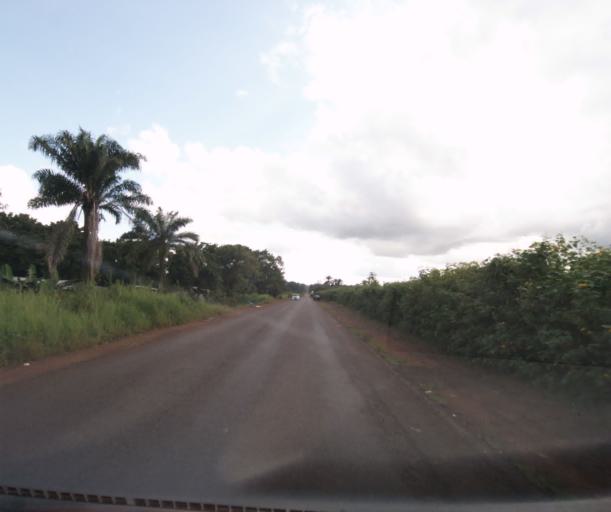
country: CM
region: West
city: Foumban
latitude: 5.6901
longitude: 10.8082
